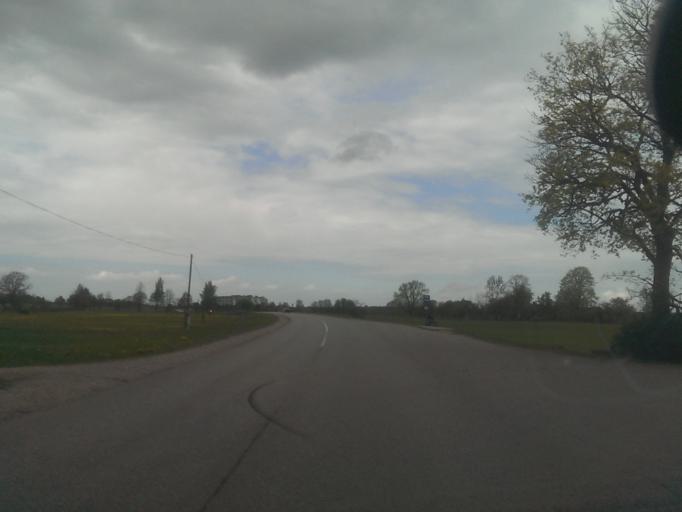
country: LV
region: Kuldigas Rajons
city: Kuldiga
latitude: 57.0059
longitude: 21.8923
